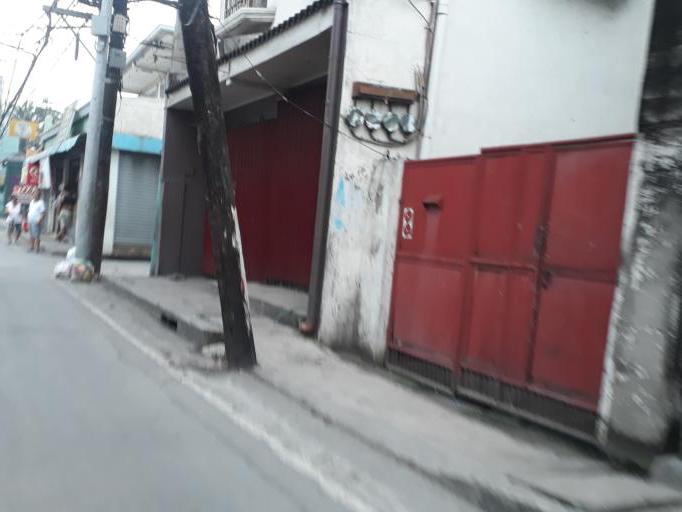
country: PH
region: Calabarzon
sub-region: Province of Rizal
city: Malabon
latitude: 14.6653
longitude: 120.9417
